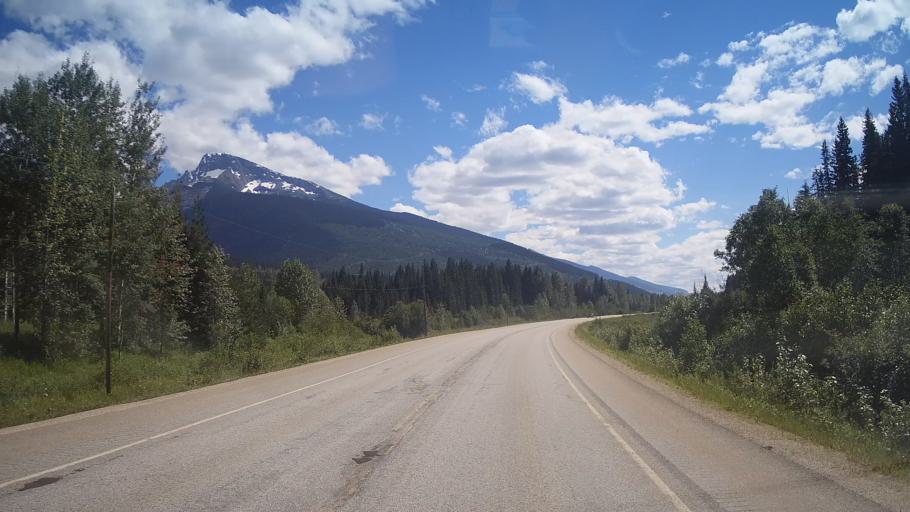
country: CA
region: Alberta
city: Jasper Park Lodge
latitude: 52.5840
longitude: -119.0956
